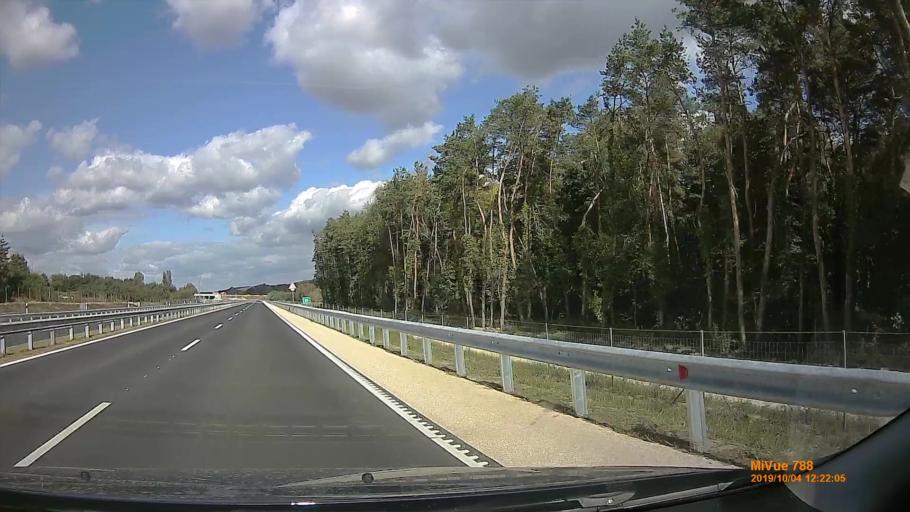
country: HU
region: Somogy
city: Karad
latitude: 46.6164
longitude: 17.7972
